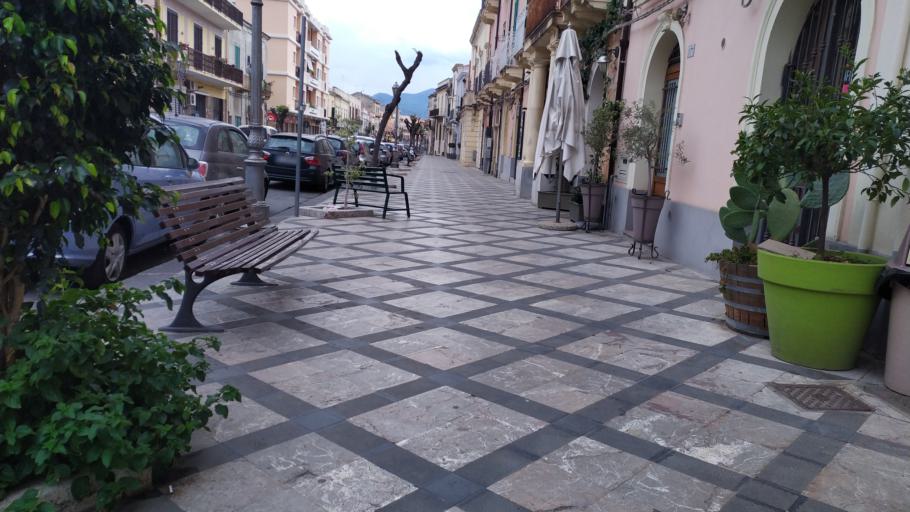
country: IT
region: Sicily
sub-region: Messina
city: Milazzo
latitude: 38.2242
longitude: 15.2406
